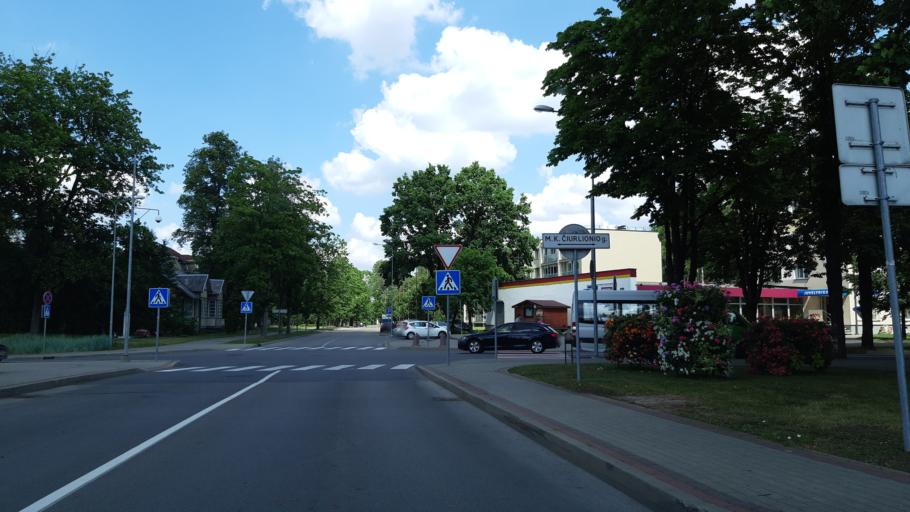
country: LT
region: Alytaus apskritis
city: Druskininkai
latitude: 54.0140
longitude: 23.9818
